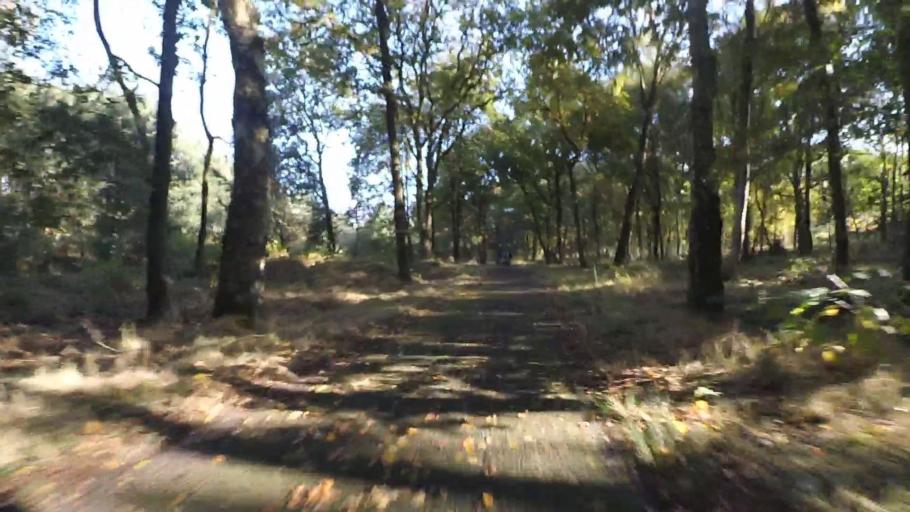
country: NL
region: Gelderland
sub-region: Gemeente Harderwijk
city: Harderwijk
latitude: 52.3379
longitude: 5.6483
